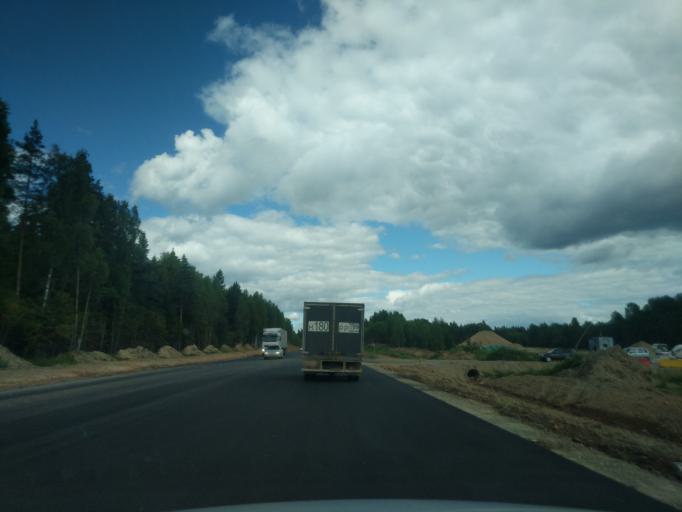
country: RU
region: Kostroma
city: Sudislavl'
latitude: 57.8212
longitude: 41.4908
